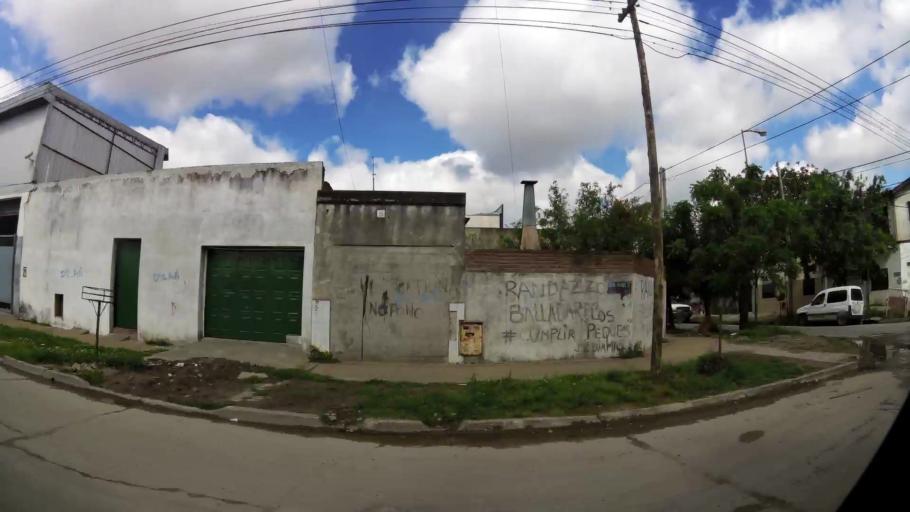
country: AR
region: Buenos Aires
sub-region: Partido de Lanus
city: Lanus
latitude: -34.6903
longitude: -58.4252
